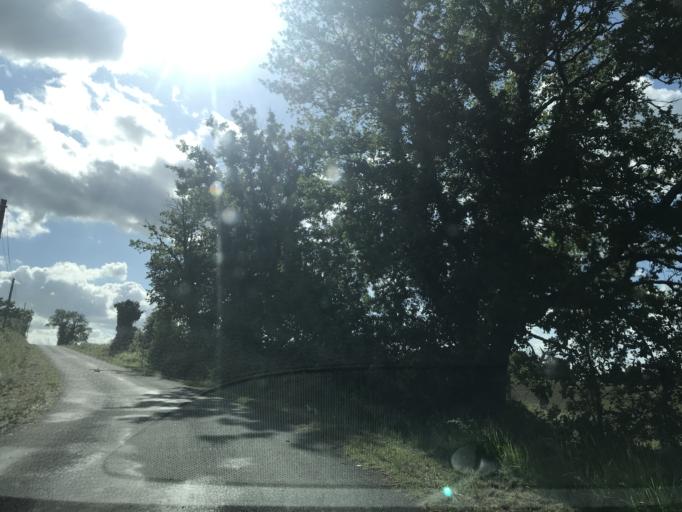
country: FR
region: Poitou-Charentes
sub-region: Departement de la Charente
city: Chalais
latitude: 45.2742
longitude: -0.0187
